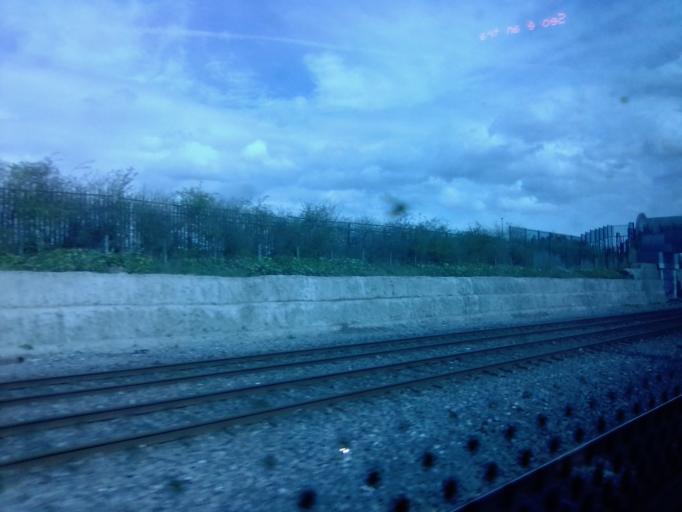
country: IE
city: Cherry Orchard
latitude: 53.3350
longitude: -6.3661
